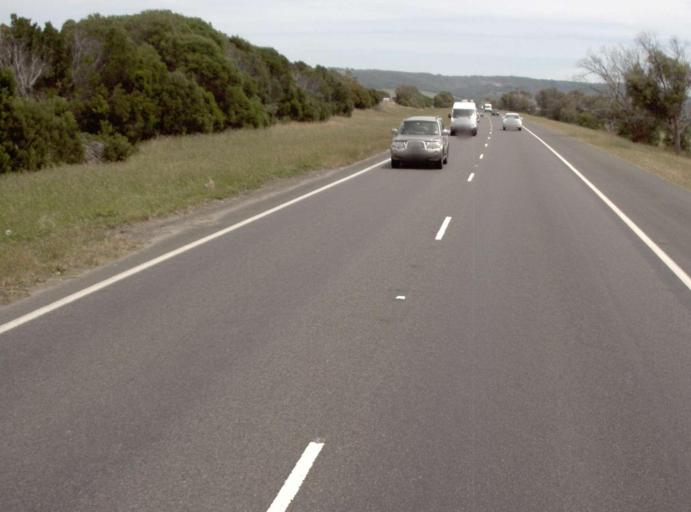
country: AU
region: Victoria
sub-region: Mornington Peninsula
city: Safety Beach
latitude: -38.3085
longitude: 145.0202
